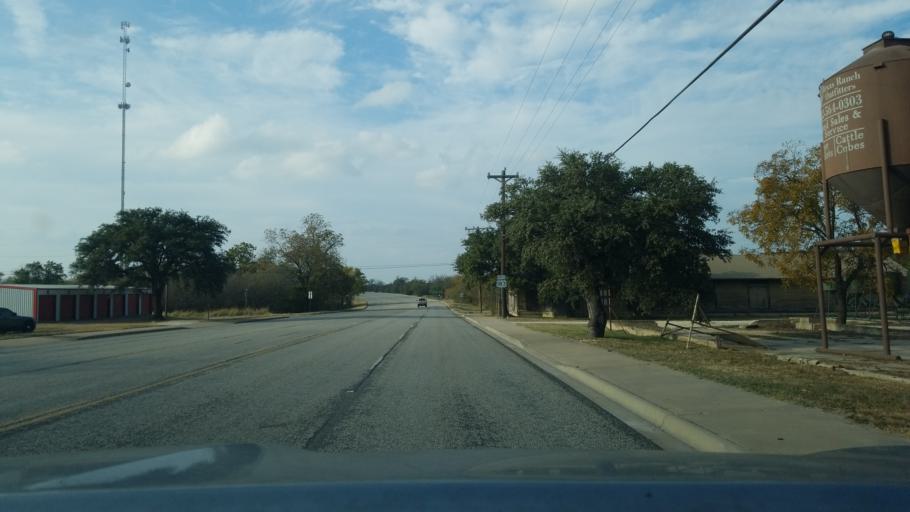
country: US
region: Texas
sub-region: Lampasas County
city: Lampasas
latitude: 31.2183
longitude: -98.3949
